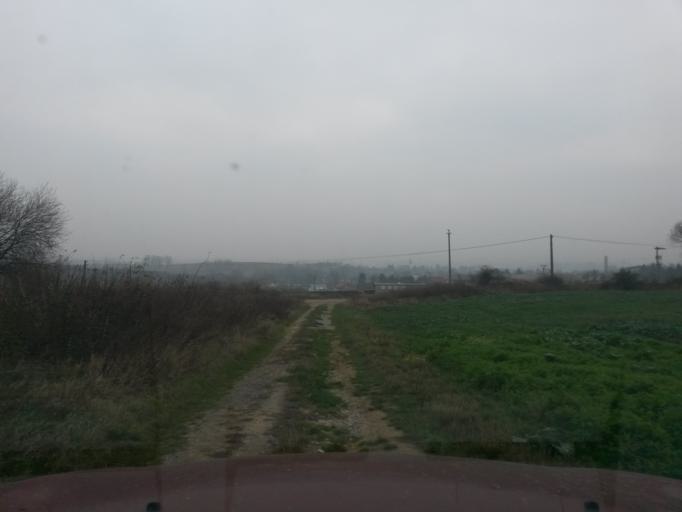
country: SK
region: Presovsky
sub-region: Okres Presov
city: Presov
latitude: 48.8837
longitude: 21.2718
